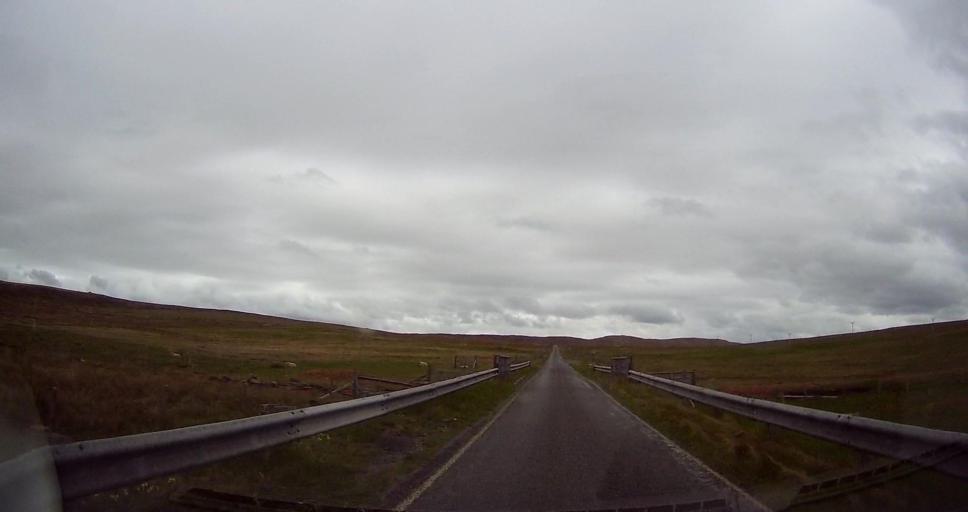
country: GB
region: Scotland
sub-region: Shetland Islands
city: Lerwick
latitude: 60.4876
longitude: -1.4899
